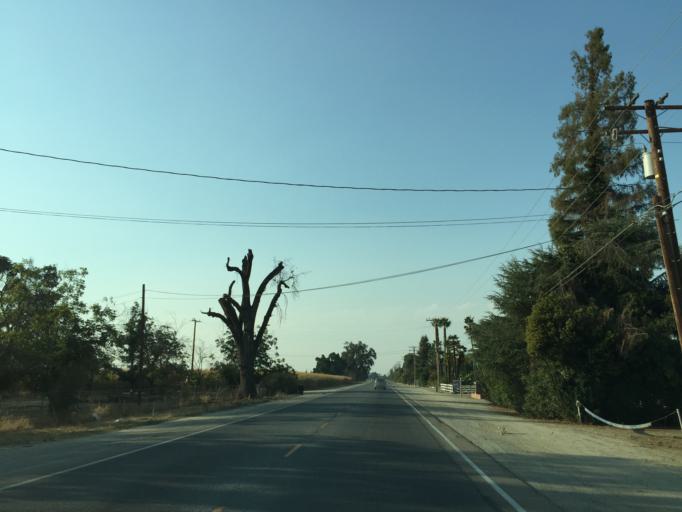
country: US
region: California
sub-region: Tulare County
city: Visalia
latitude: 36.3583
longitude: -119.2790
